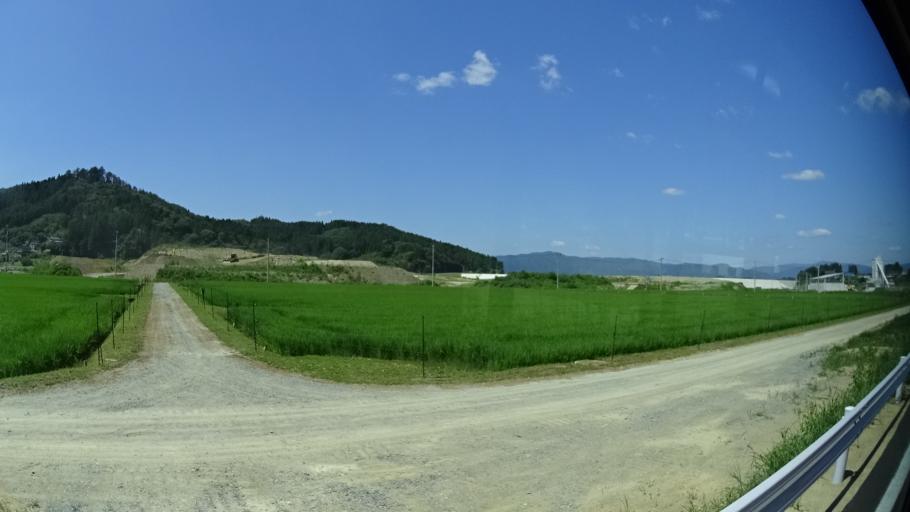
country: JP
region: Iwate
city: Ofunato
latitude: 38.9954
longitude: 141.6904
